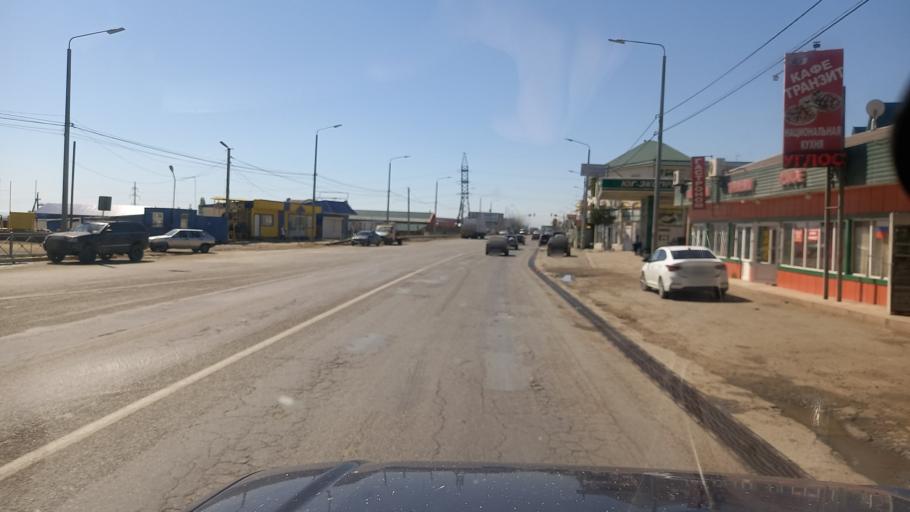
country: RU
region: Dagestan
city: Derbent
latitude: 42.0352
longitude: 48.2942
